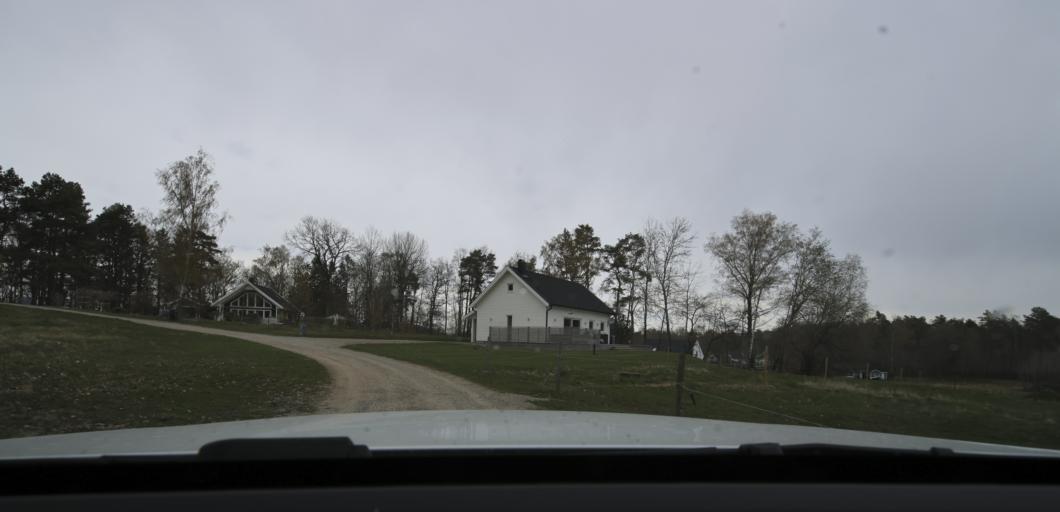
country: SE
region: Halland
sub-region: Varbergs Kommun
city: Tvaaker
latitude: 57.1260
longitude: 12.4598
